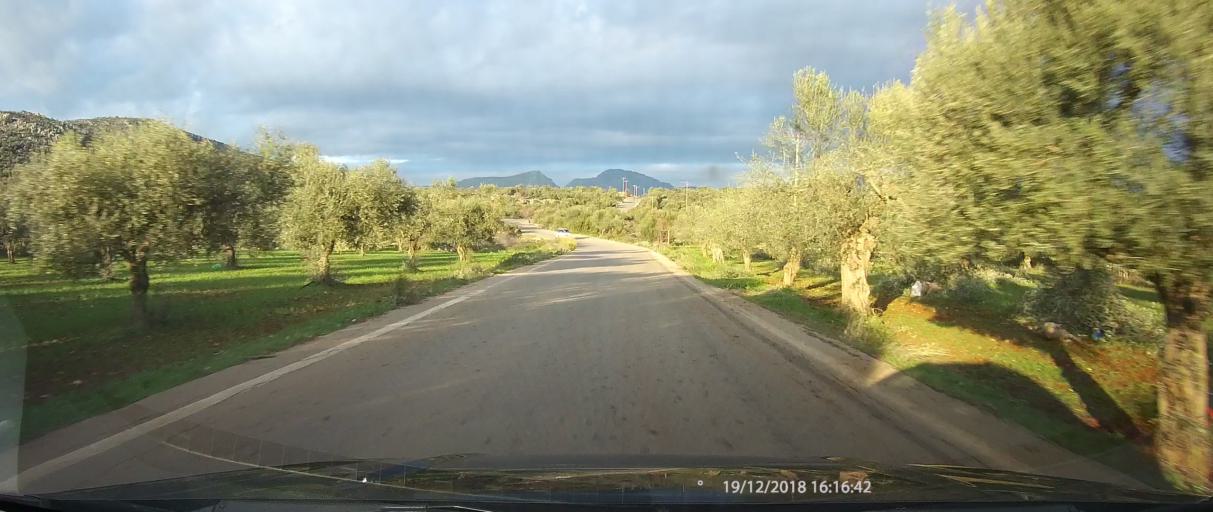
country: GR
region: Peloponnese
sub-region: Nomos Lakonias
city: Kato Glikovrisi
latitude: 36.9031
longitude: 22.8056
